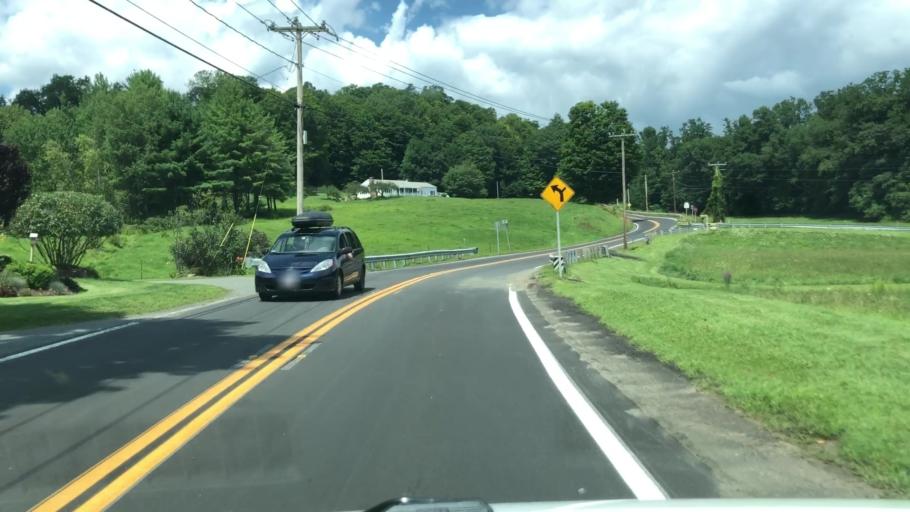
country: US
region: Massachusetts
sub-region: Franklin County
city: Ashfield
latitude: 42.5206
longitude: -72.7825
